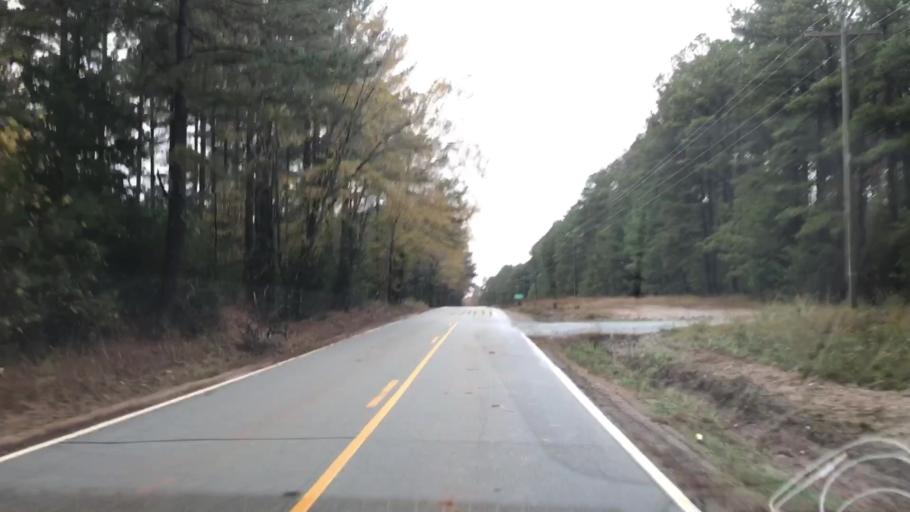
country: US
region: South Carolina
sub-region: Greenwood County
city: Ninety Six
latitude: 34.3075
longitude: -81.9669
